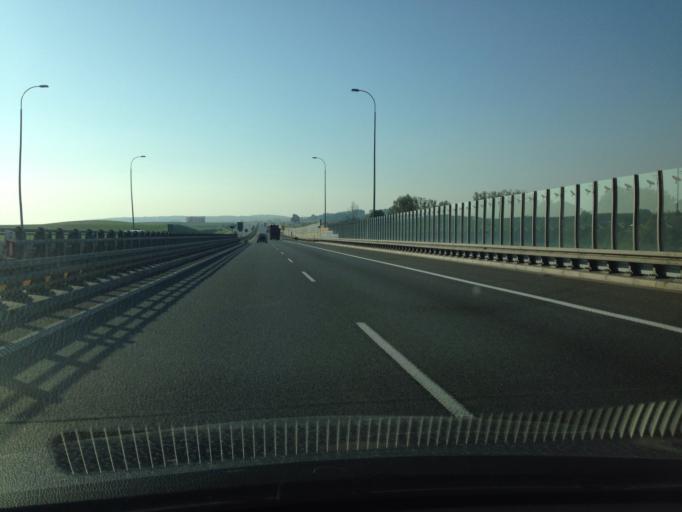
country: PL
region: Pomeranian Voivodeship
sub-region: Powiat gdanski
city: Legowo
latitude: 54.2226
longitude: 18.6129
